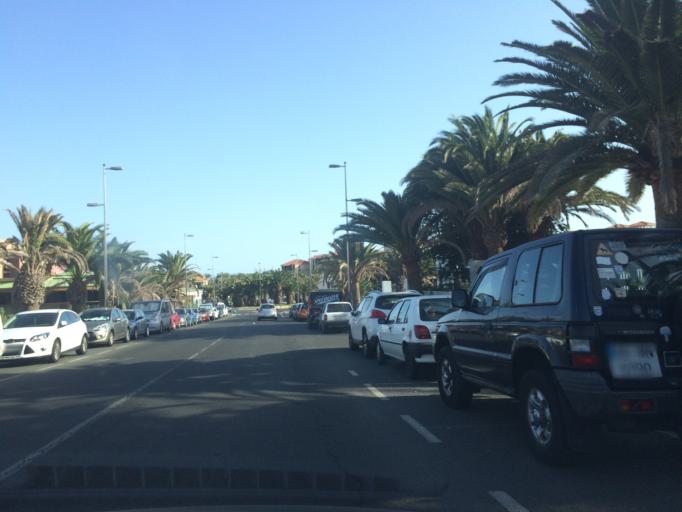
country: ES
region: Canary Islands
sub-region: Provincia de Las Palmas
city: Maspalomas
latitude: 27.7404
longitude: -15.6023
